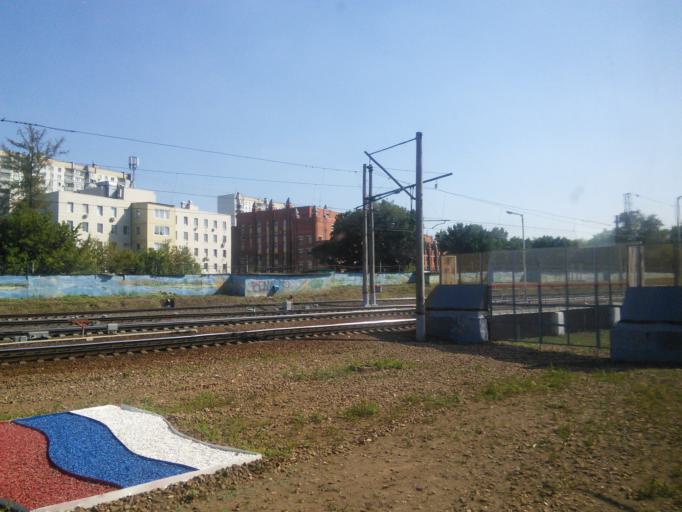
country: RU
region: Moscow
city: Tekstil'shchiki
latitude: 55.6868
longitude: 37.7347
